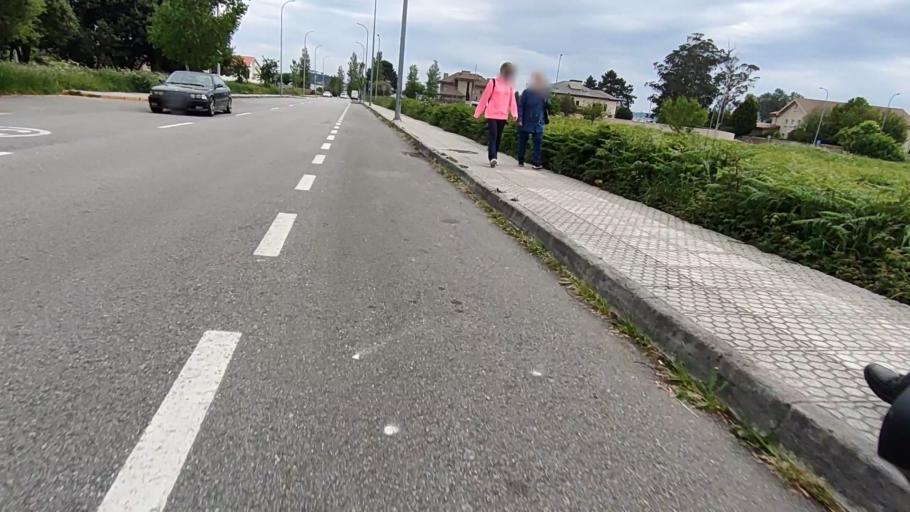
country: ES
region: Galicia
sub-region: Provincia da Coruna
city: Boiro
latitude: 42.6428
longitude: -8.8868
